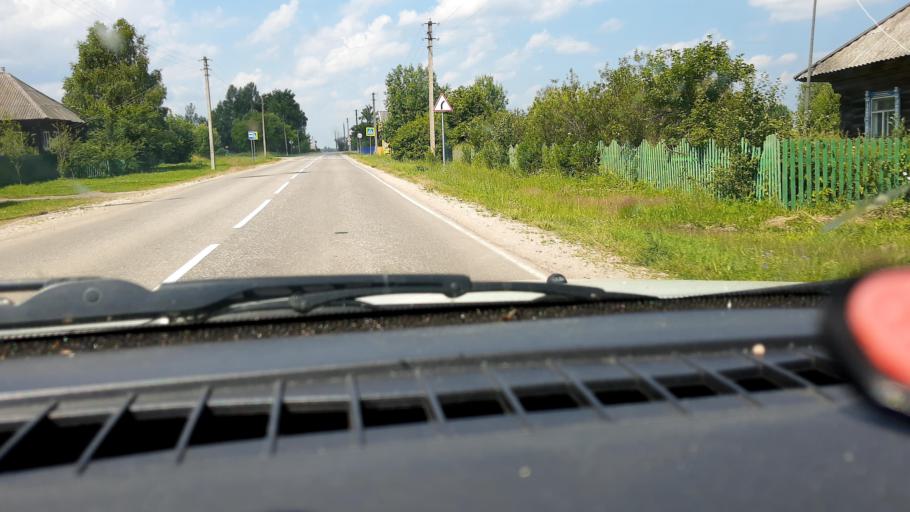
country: RU
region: Nizjnij Novgorod
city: Sharanga
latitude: 57.1276
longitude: 46.5120
